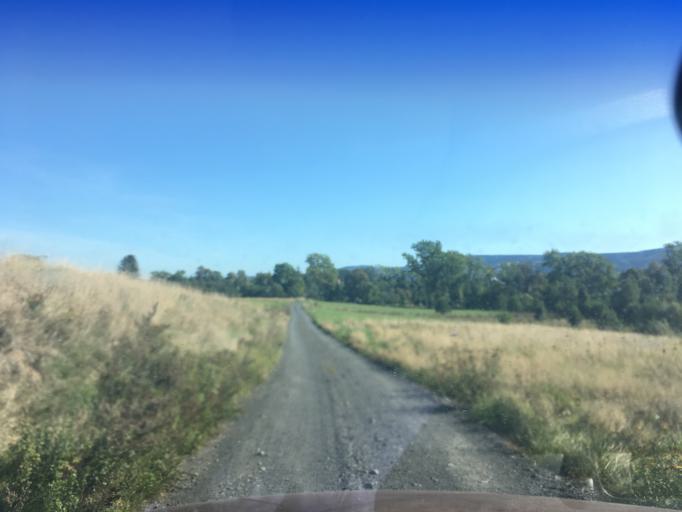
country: PL
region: Lower Silesian Voivodeship
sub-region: Powiat lubanski
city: Swieradow-Zdroj
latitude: 50.9634
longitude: 15.3189
